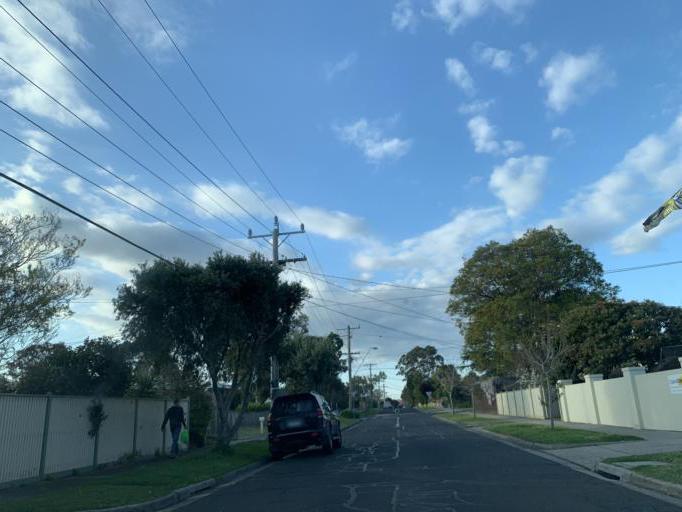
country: AU
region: Victoria
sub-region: Kingston
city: Parkdale
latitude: -37.9831
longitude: 145.0844
